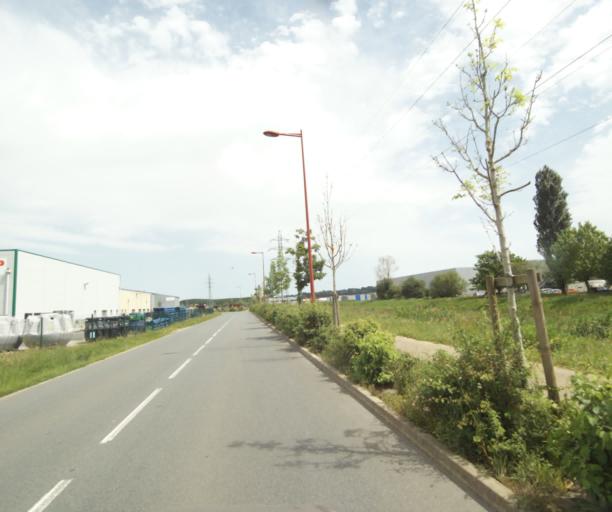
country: FR
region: Aquitaine
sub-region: Departement des Pyrenees-Atlantiques
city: Mouguerre
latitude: 43.4898
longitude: -1.4262
